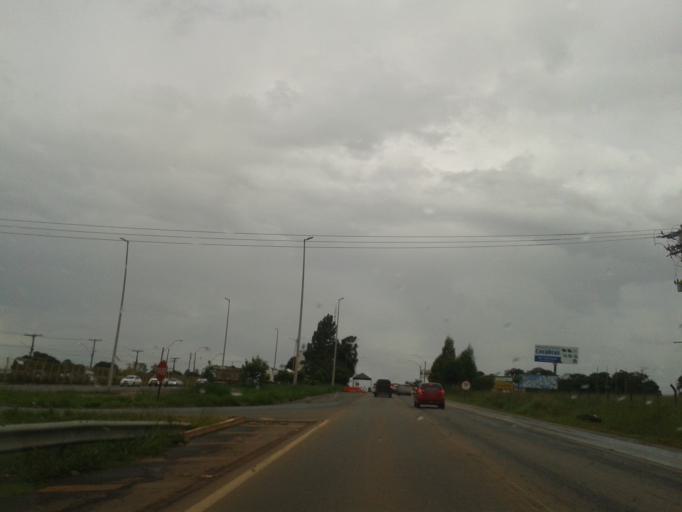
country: BR
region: Goias
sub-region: Goiania
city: Goiania
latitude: -16.6182
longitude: -49.3590
